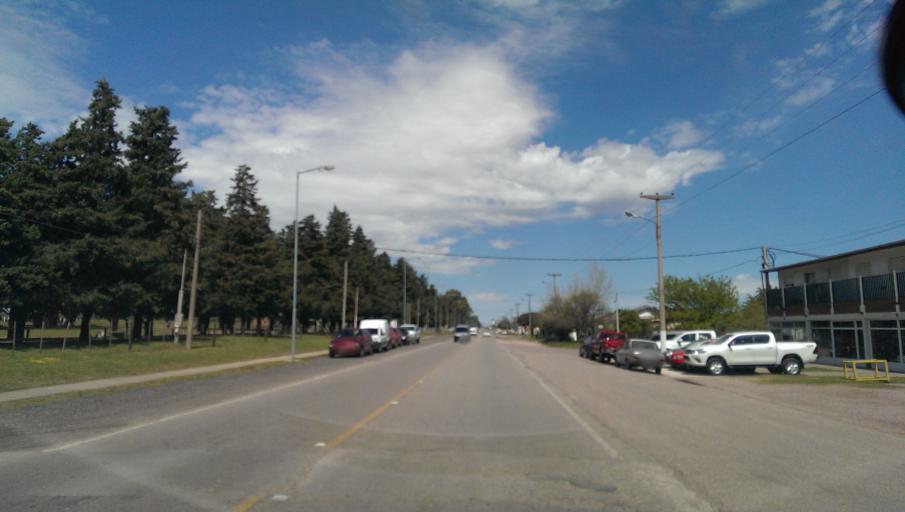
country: AR
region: Buenos Aires
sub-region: Partido de Tornquist
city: Tornquist
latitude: -38.0937
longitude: -62.2186
